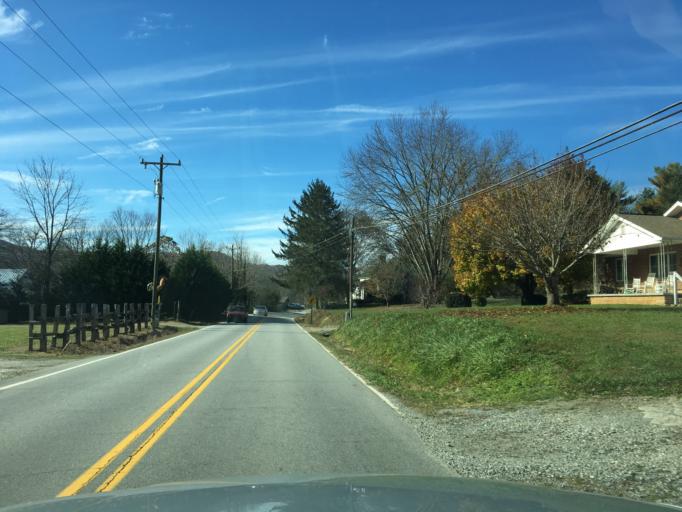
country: US
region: North Carolina
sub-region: Henderson County
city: Etowah
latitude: 35.2378
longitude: -82.6265
